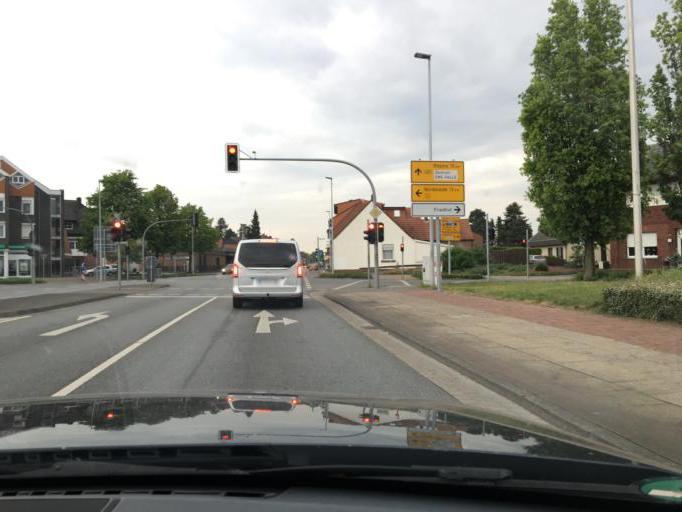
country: DE
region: North Rhine-Westphalia
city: Emsdetten
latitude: 52.1675
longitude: 7.5417
